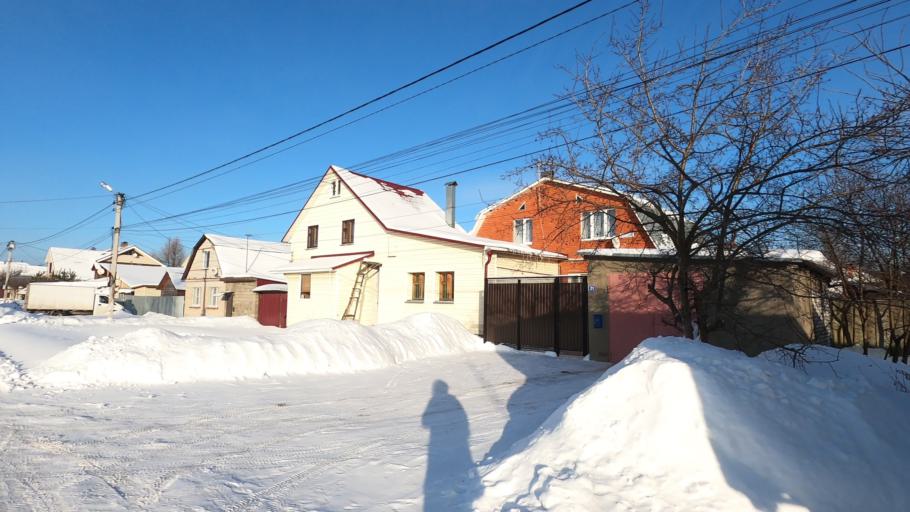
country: RU
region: Moskovskaya
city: Pavlovskiy Posad
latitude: 55.7694
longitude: 38.6981
